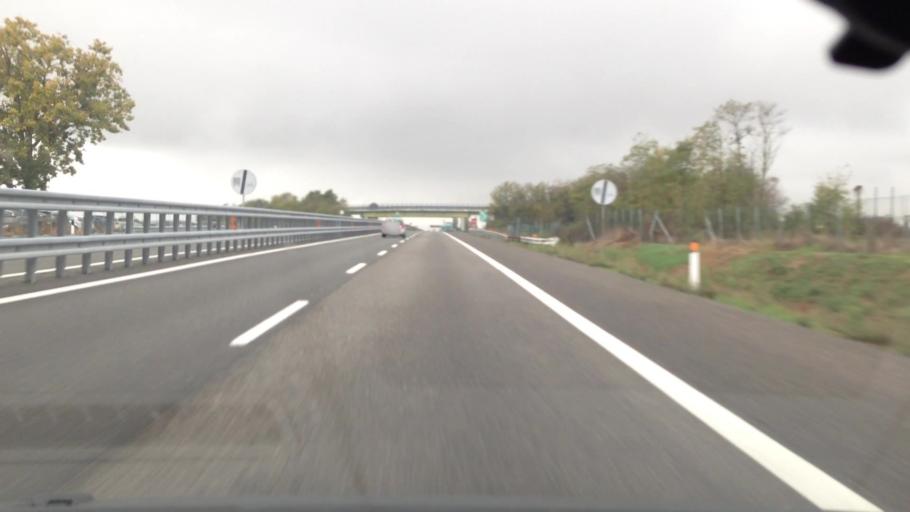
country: IT
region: Piedmont
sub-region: Provincia di Asti
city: San Paolo Solbrito
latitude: 44.9485
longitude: 7.9651
